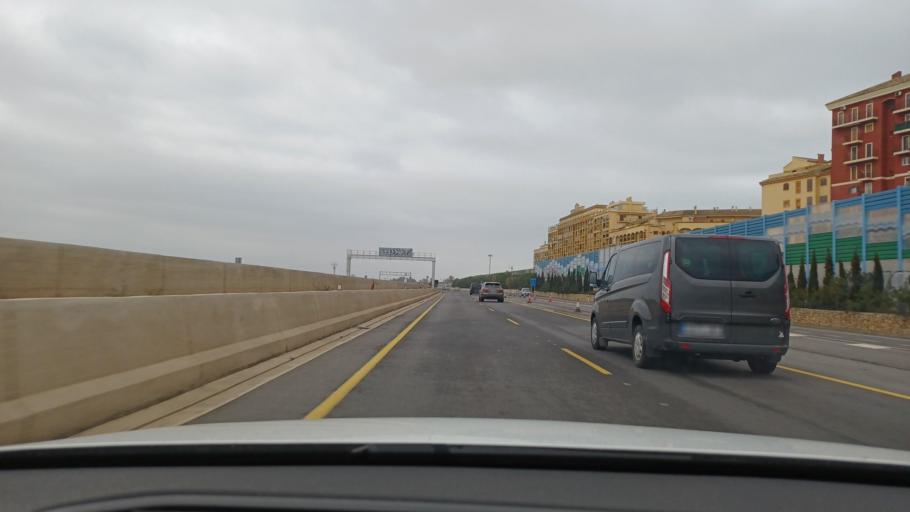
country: ES
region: Valencia
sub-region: Provincia de Valencia
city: Meliana
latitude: 39.5120
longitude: -0.3230
